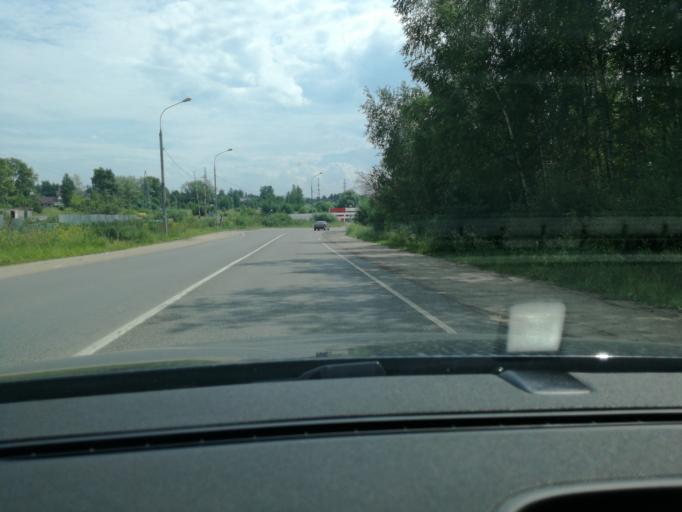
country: RU
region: Moskovskaya
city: Dmitrov
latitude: 56.3392
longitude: 37.5544
